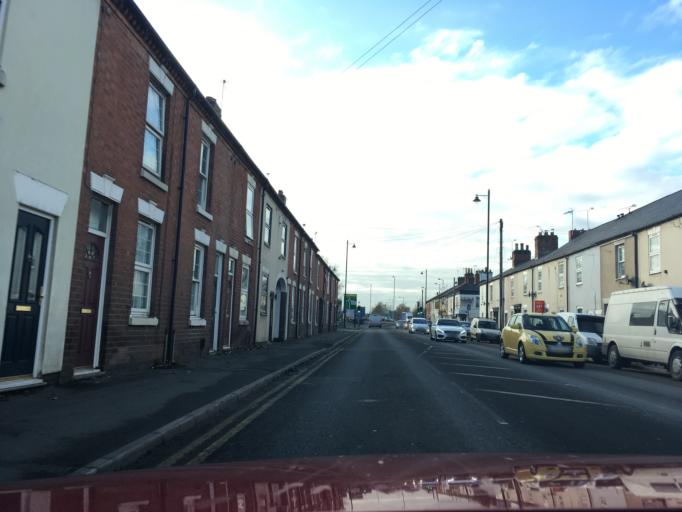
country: GB
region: England
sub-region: Staffordshire
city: Burton upon Trent
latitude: 52.8059
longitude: -1.6469
